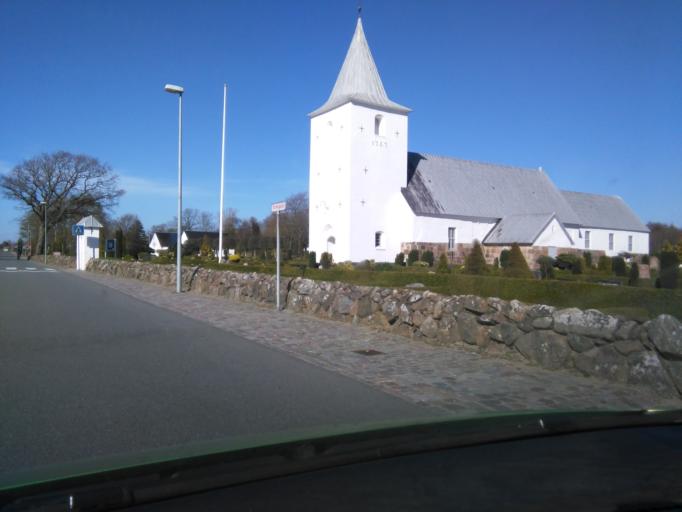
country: DK
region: South Denmark
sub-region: Varde Kommune
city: Oksbol
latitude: 55.6312
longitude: 8.2806
